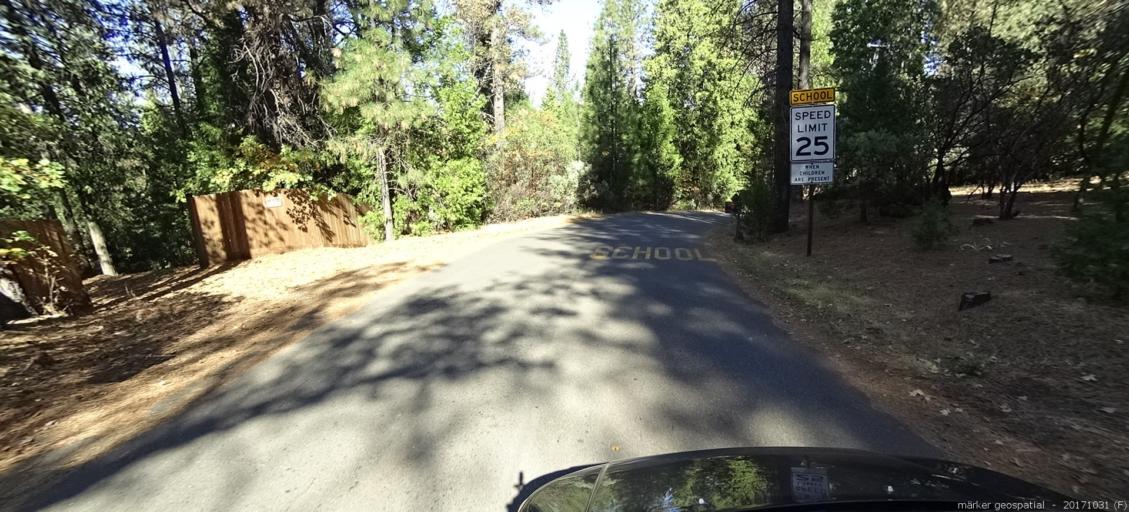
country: US
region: California
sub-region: Shasta County
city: Shingletown
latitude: 40.5107
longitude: -121.9374
